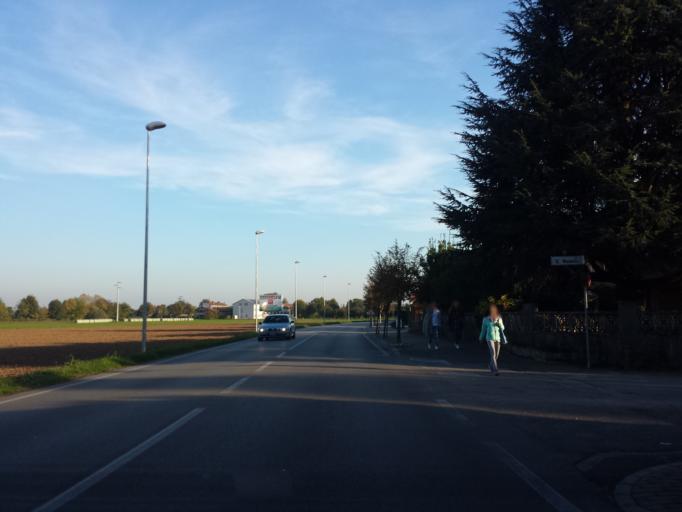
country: IT
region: Veneto
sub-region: Provincia di Vicenza
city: Crispi Cavour
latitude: 45.5883
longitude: 11.5304
